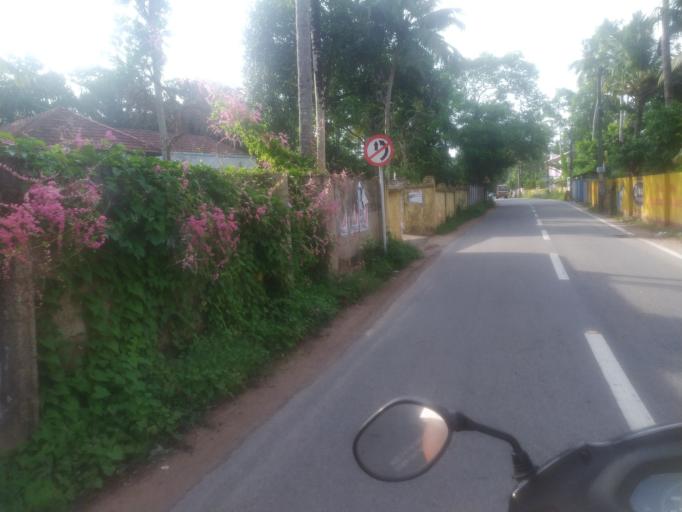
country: IN
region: Kerala
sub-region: Thiruvananthapuram
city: Attingal
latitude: 8.6171
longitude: 76.8279
